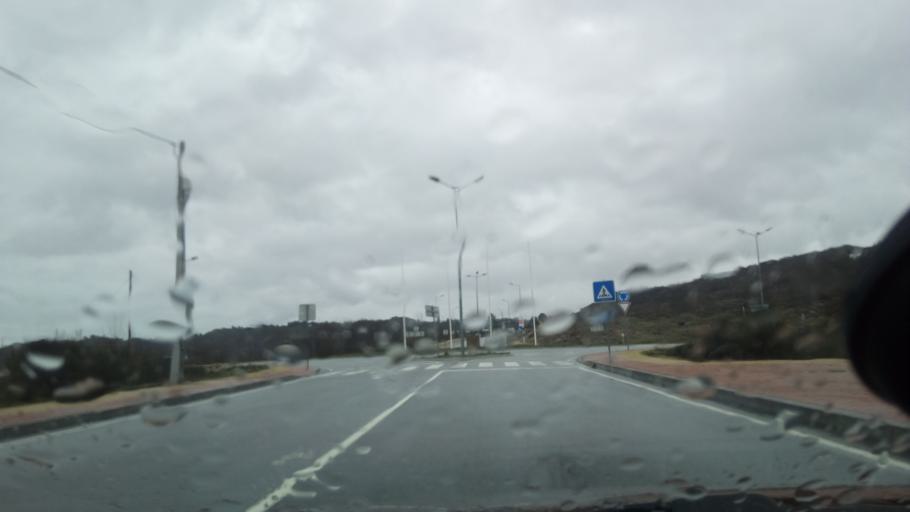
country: PT
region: Guarda
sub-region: Celorico da Beira
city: Celorico da Beira
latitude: 40.6257
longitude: -7.4193
